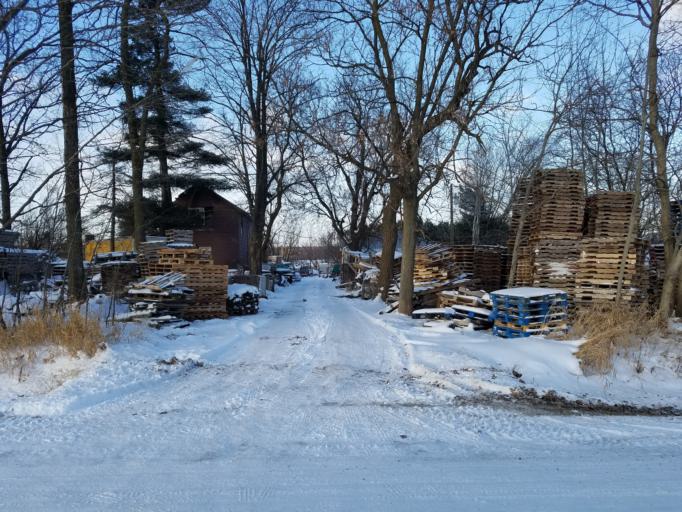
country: US
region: Wisconsin
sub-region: Clark County
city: Loyal
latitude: 44.6314
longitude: -90.4561
